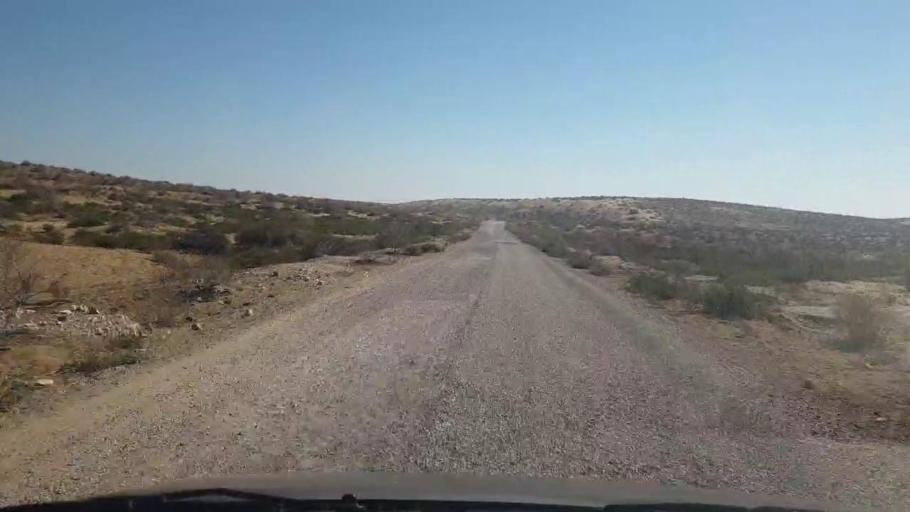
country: PK
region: Sindh
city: Bozdar
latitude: 27.0170
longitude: 68.7349
